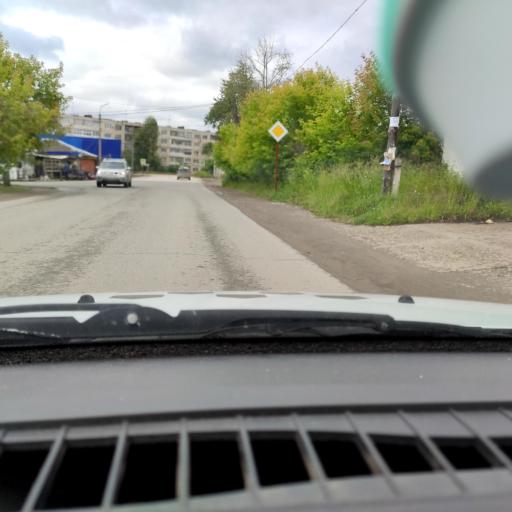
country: RU
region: Perm
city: Dobryanka
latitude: 58.4678
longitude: 56.4099
